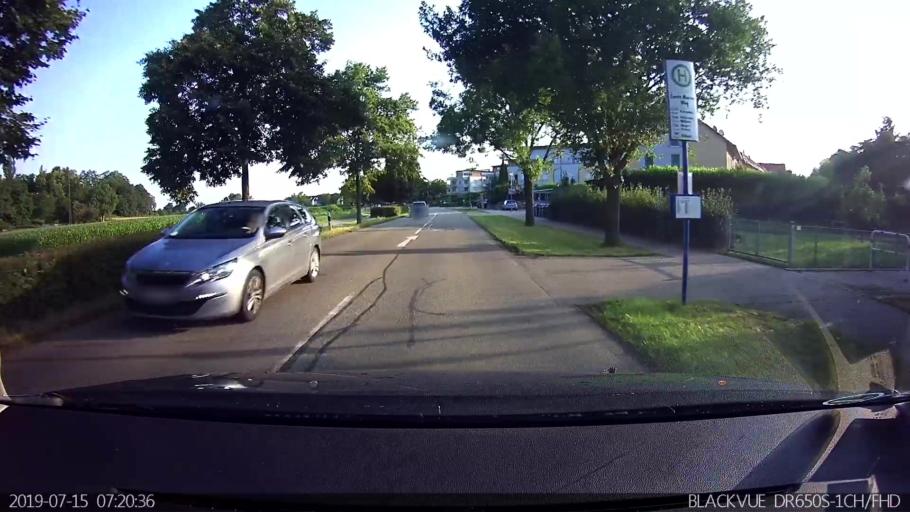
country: DE
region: Baden-Wuerttemberg
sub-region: Freiburg Region
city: Unterkrozingen
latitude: 47.9225
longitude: 7.6851
